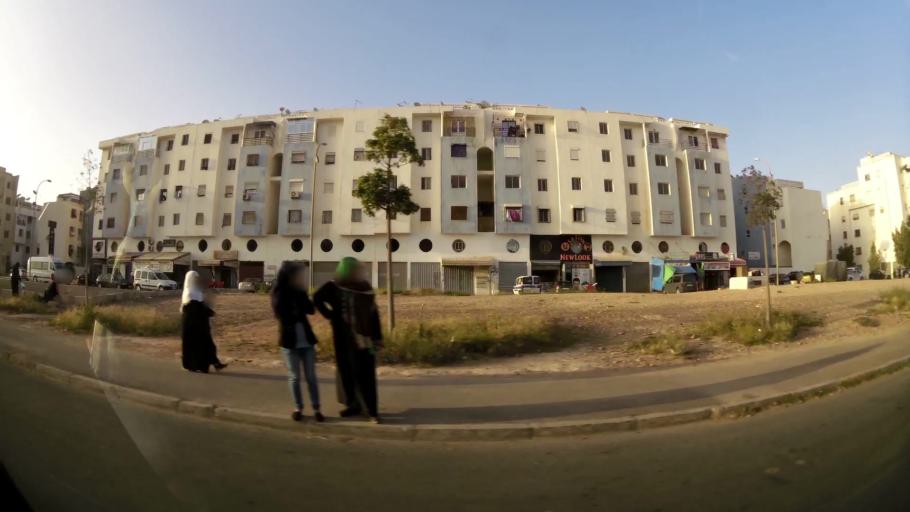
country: MA
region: Oued ed Dahab-Lagouira
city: Dakhla
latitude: 30.3907
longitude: -9.5630
